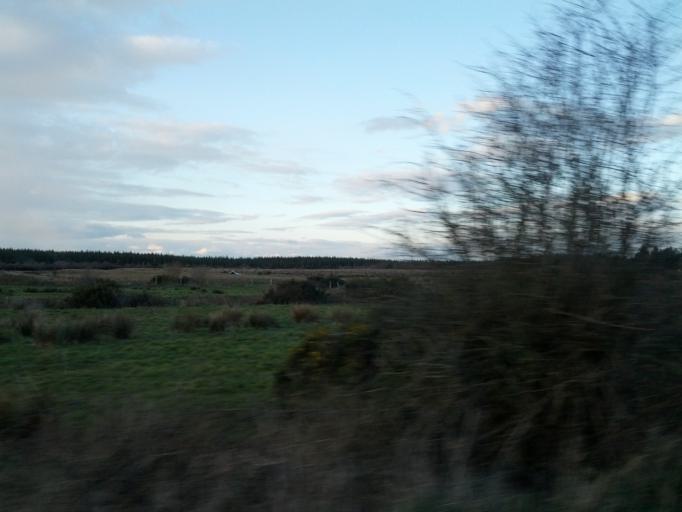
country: IE
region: Connaught
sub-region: County Galway
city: Athenry
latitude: 53.3266
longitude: -8.6457
